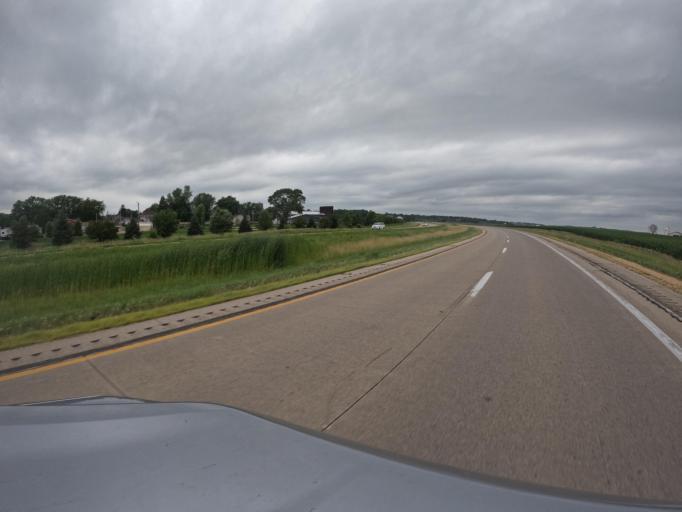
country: US
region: Iowa
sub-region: Clinton County
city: De Witt
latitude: 41.9095
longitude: -90.5910
